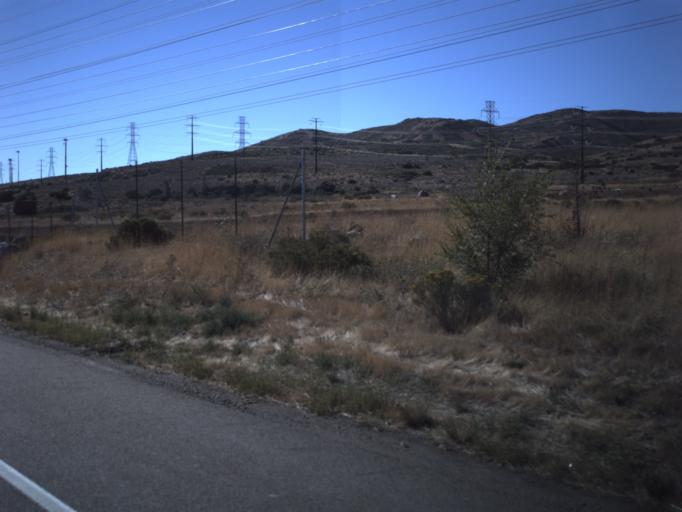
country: US
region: Utah
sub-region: Salt Lake County
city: Bluffdale
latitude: 40.4647
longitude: -111.9439
